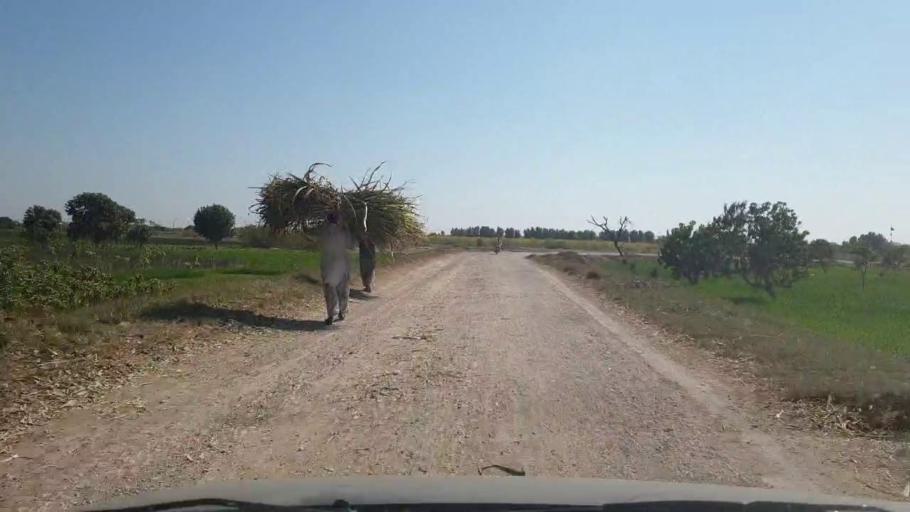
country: PK
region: Sindh
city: Mirwah Gorchani
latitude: 25.3006
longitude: 69.1241
